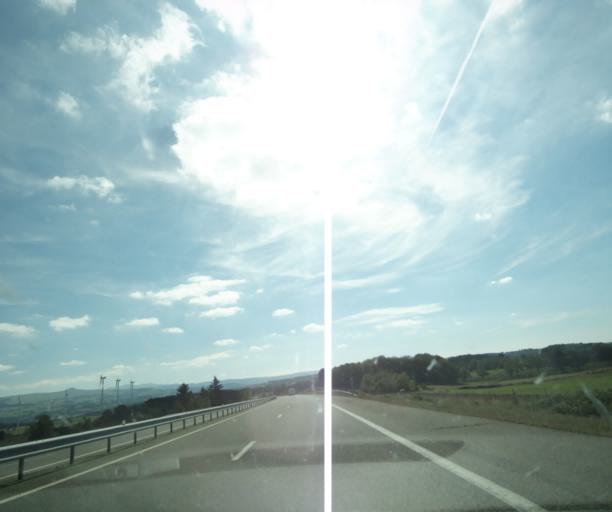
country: FR
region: Auvergne
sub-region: Departement du Puy-de-Dome
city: Saint-Sauves-d'Auvergne
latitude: 45.6969
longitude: 2.6943
